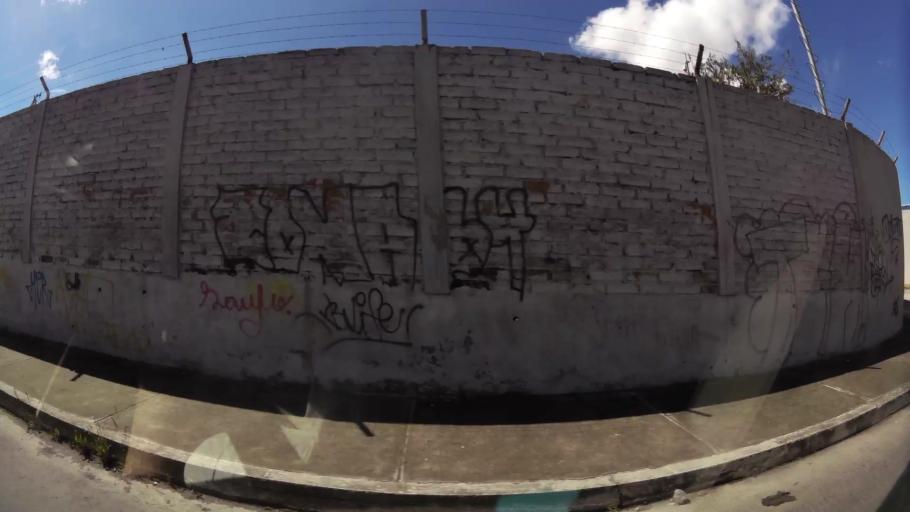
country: EC
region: Pichincha
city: Quito
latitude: -0.2956
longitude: -78.5433
